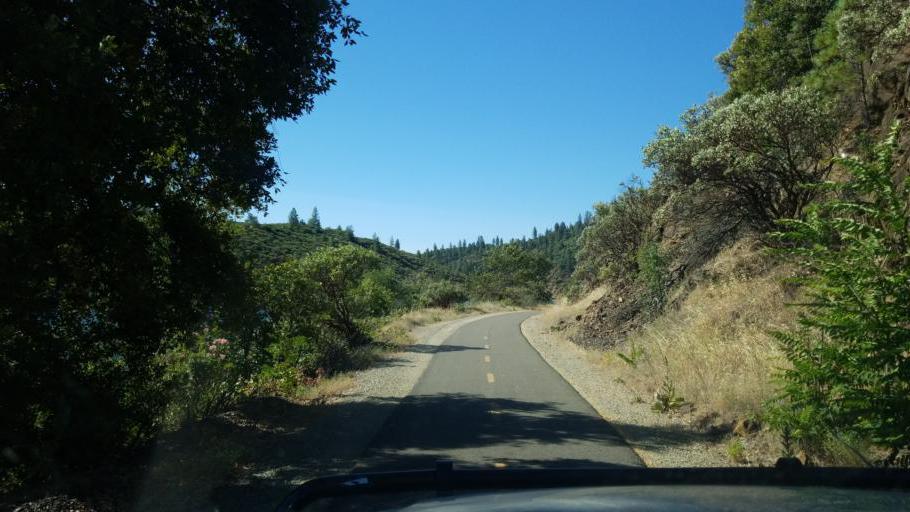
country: US
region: California
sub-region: Shasta County
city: Shasta
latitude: 40.6677
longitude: -122.4605
